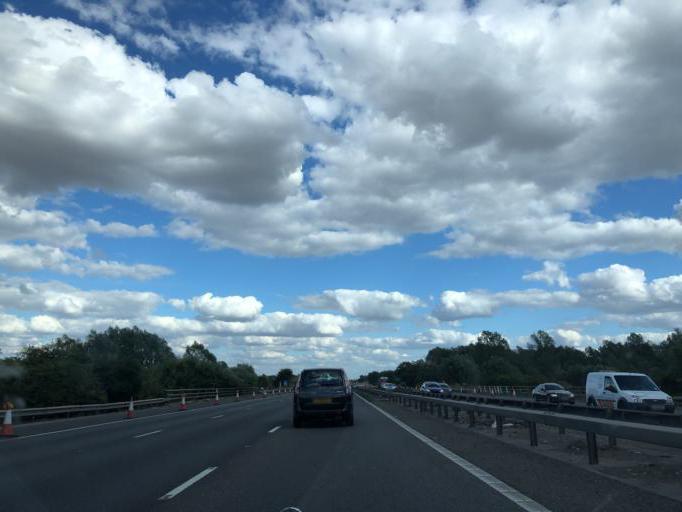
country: GB
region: England
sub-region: Milton Keynes
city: Broughton
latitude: 52.0640
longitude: -0.7123
